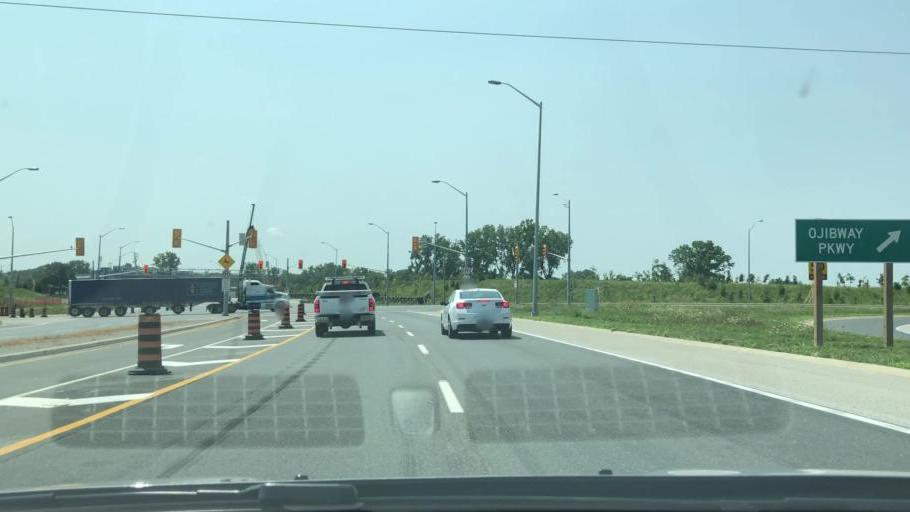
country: US
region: Michigan
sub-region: Wayne County
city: River Rouge
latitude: 42.2748
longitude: -83.0780
